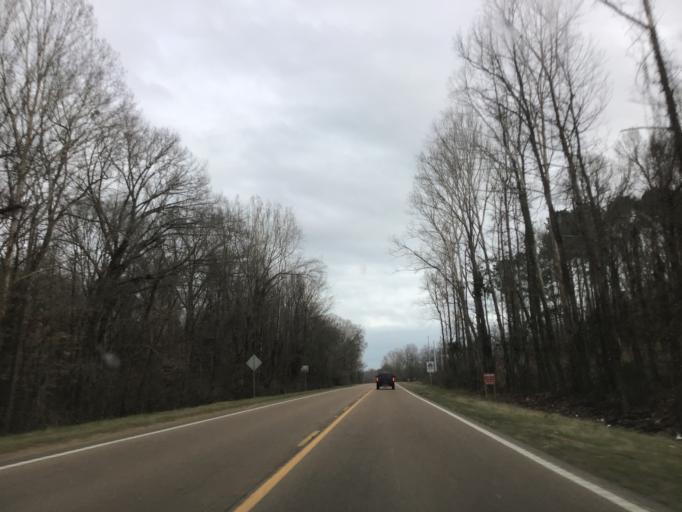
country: US
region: Mississippi
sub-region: Warren County
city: Beechwood
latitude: 32.3151
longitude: -90.8102
